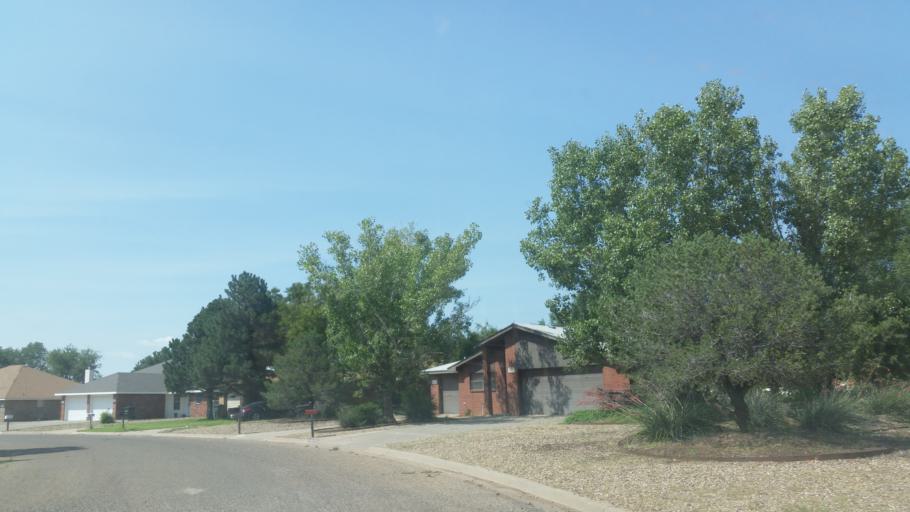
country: US
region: New Mexico
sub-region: Curry County
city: Clovis
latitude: 34.4424
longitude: -103.1929
